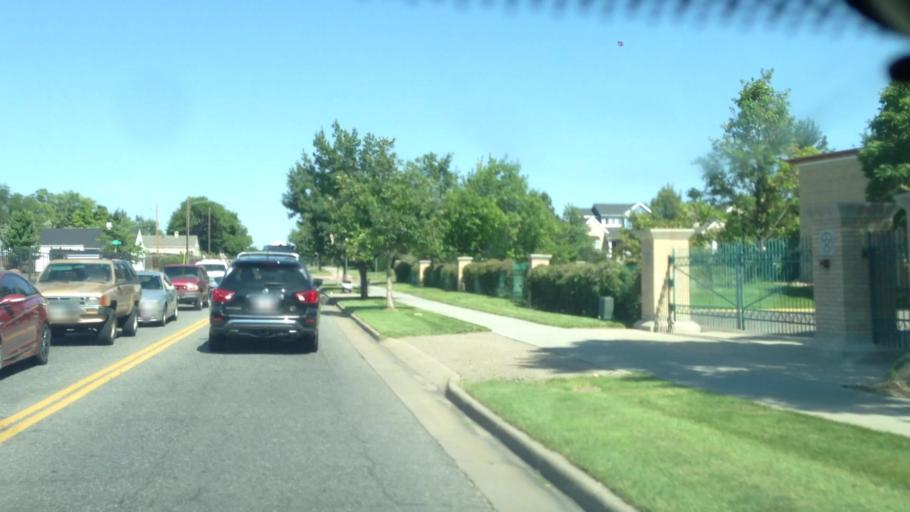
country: US
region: Colorado
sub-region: Arapahoe County
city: Glendale
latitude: 39.7328
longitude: -104.9031
